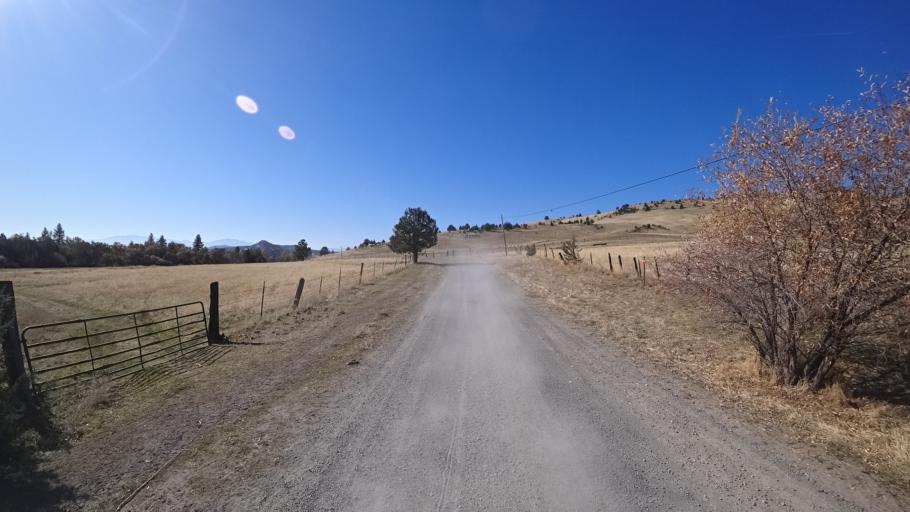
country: US
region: California
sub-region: Siskiyou County
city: Montague
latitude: 41.7367
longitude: -122.3471
